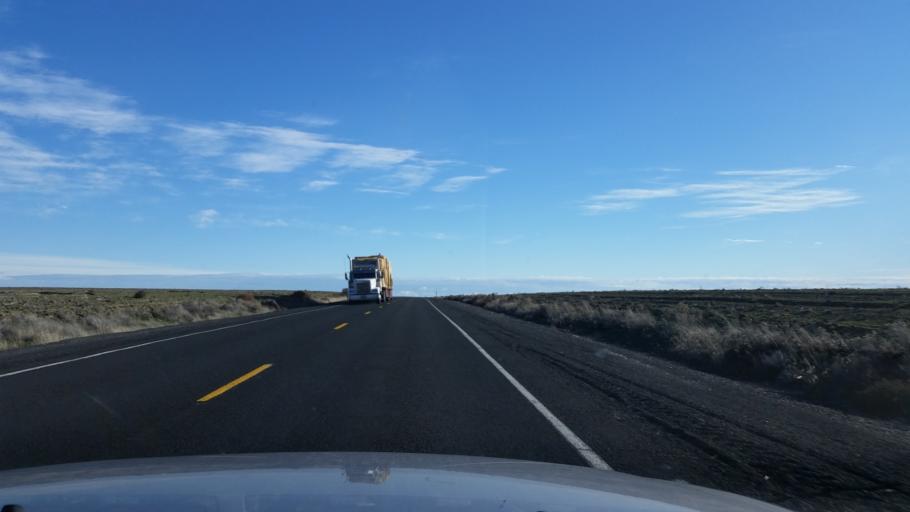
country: US
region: Washington
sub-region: Grant County
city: Warden
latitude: 47.3521
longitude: -118.9404
